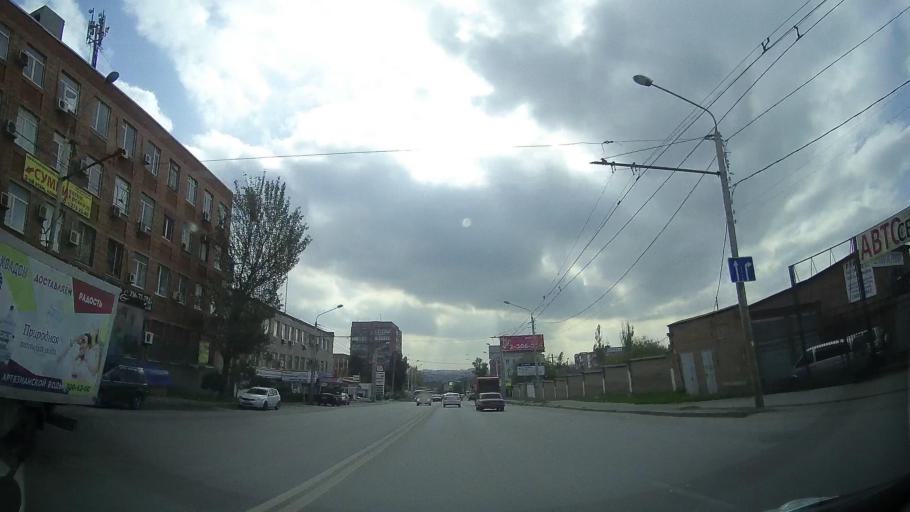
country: RU
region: Rostov
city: Severnyy
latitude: 47.2674
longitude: 39.6834
